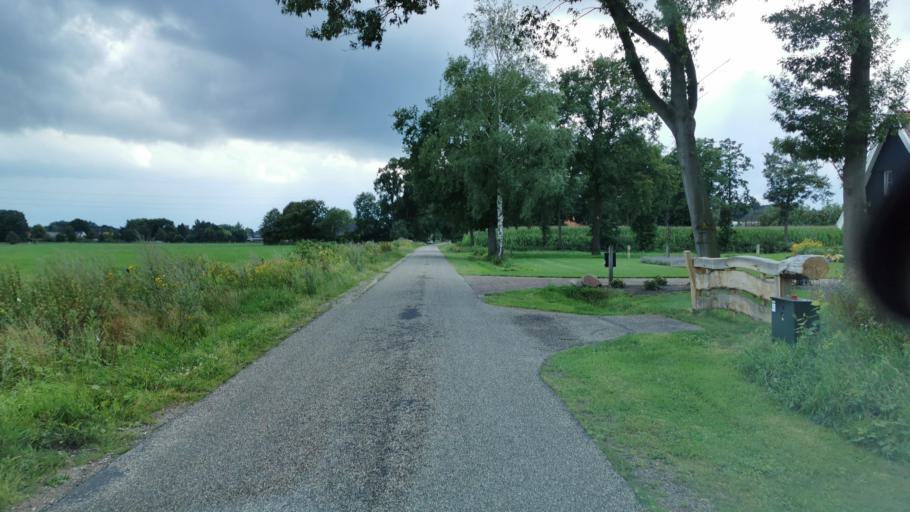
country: NL
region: Overijssel
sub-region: Gemeente Losser
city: Losser
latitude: 52.2304
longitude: 6.9761
